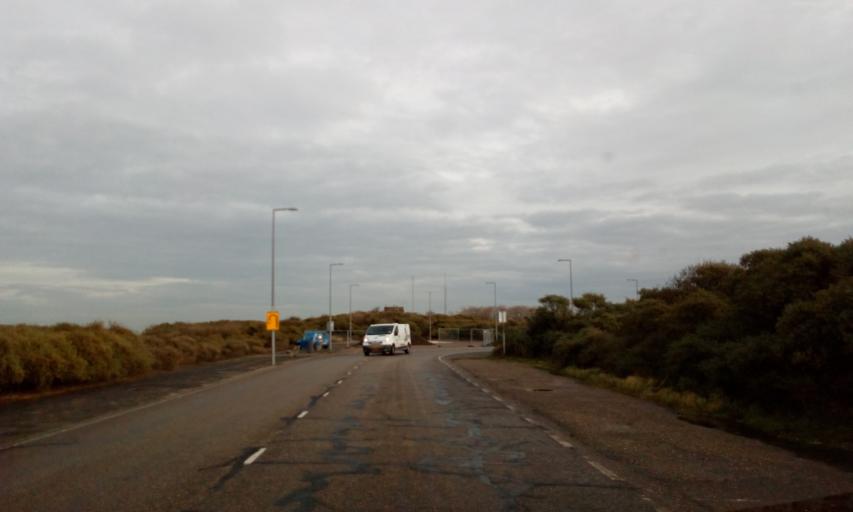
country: NL
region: South Holland
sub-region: Gemeente Rotterdam
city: Hoek van Holland
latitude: 51.9889
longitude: 4.1190
